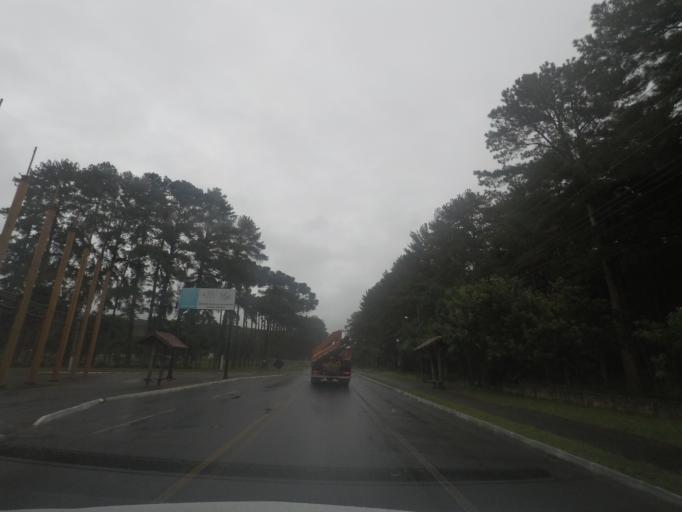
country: BR
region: Parana
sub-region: Quatro Barras
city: Quatro Barras
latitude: -25.3809
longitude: -49.1249
